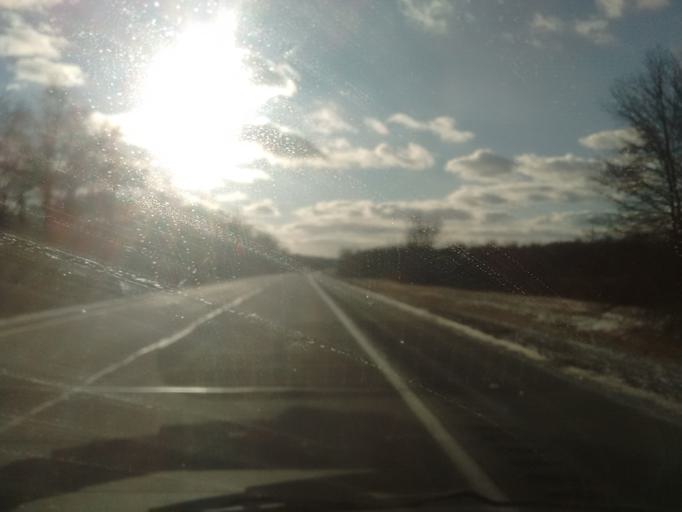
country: US
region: New York
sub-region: Orange County
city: Mechanicstown
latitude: 41.4267
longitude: -74.3950
